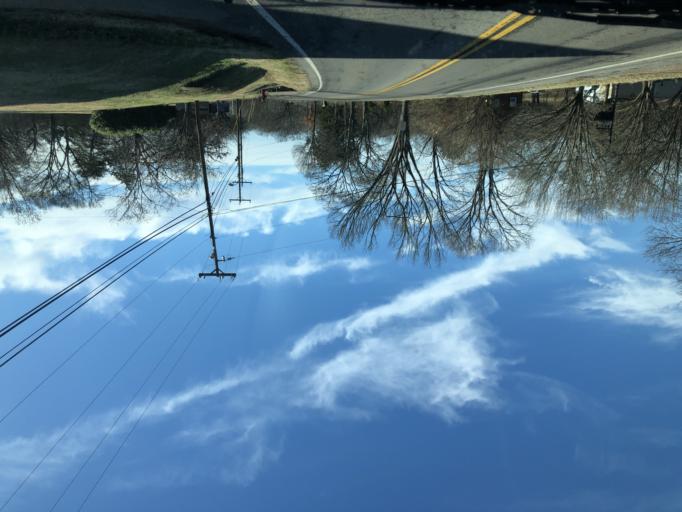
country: US
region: Tennessee
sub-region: Wilson County
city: Green Hill
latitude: 36.1738
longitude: -86.5760
